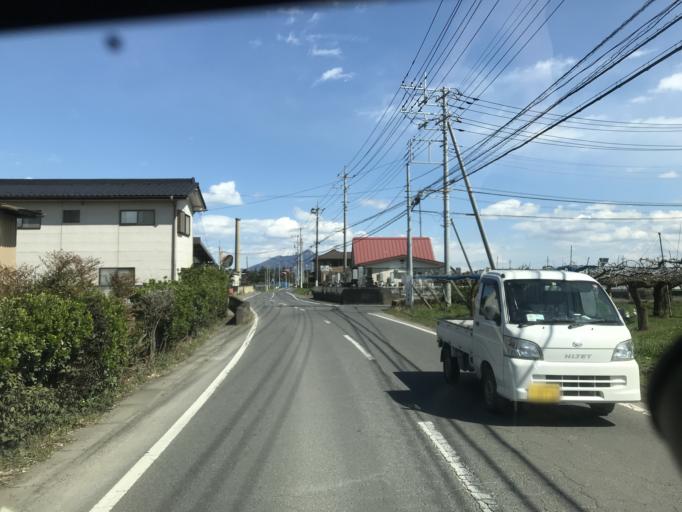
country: JP
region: Ibaraki
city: Shimodate
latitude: 36.2337
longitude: 139.9486
